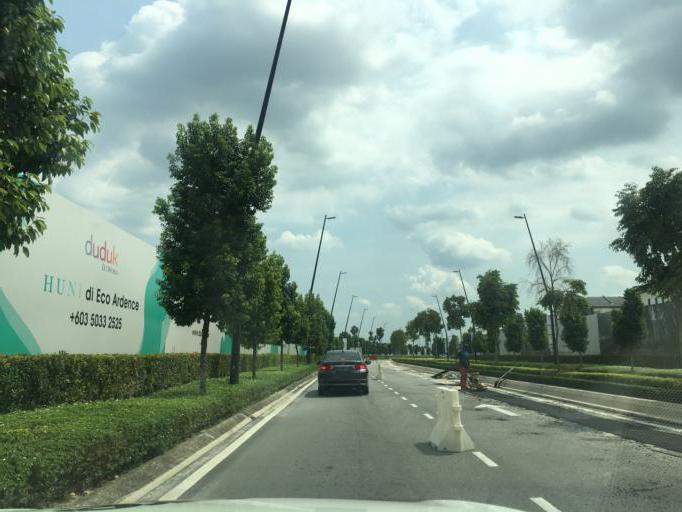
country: MY
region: Selangor
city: Shah Alam
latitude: 3.0949
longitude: 101.4754
